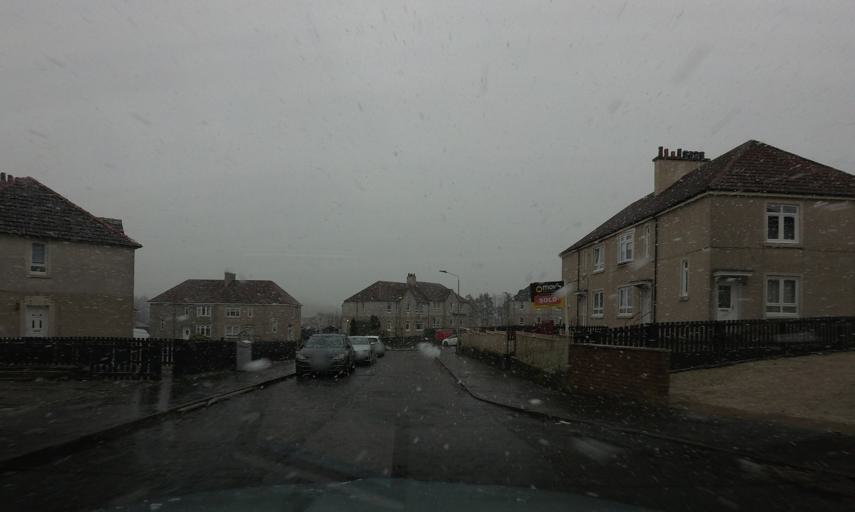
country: GB
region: Scotland
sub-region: North Lanarkshire
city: Caldercruix
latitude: 55.8425
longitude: -3.8689
